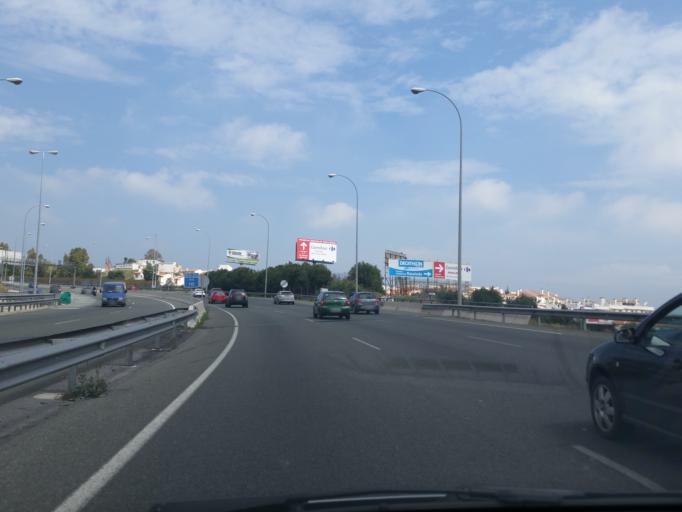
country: ES
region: Andalusia
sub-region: Provincia de Malaga
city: Malaga
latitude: 36.7253
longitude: -4.4539
